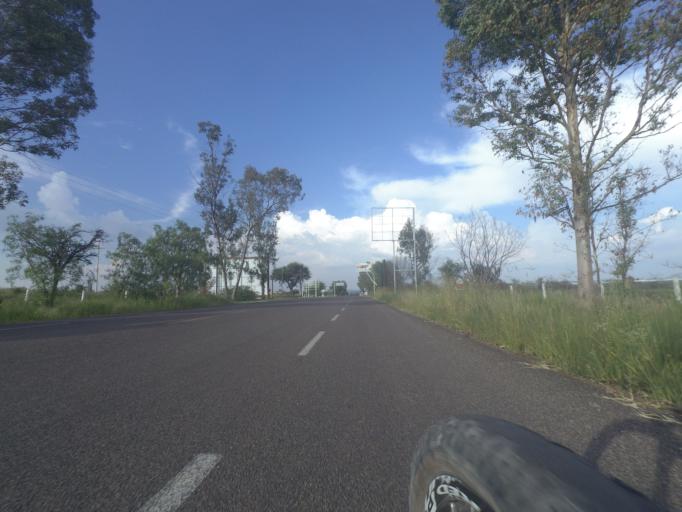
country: MX
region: Aguascalientes
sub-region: Aguascalientes
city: Penuelas (El Cienegal)
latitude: 21.7344
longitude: -102.3553
